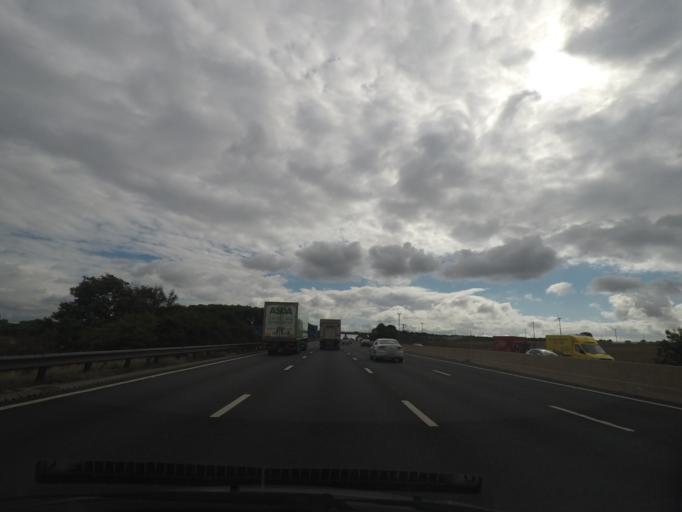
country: GB
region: England
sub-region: City and Borough of Wakefield
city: Ossett
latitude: 53.6922
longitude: -1.5570
